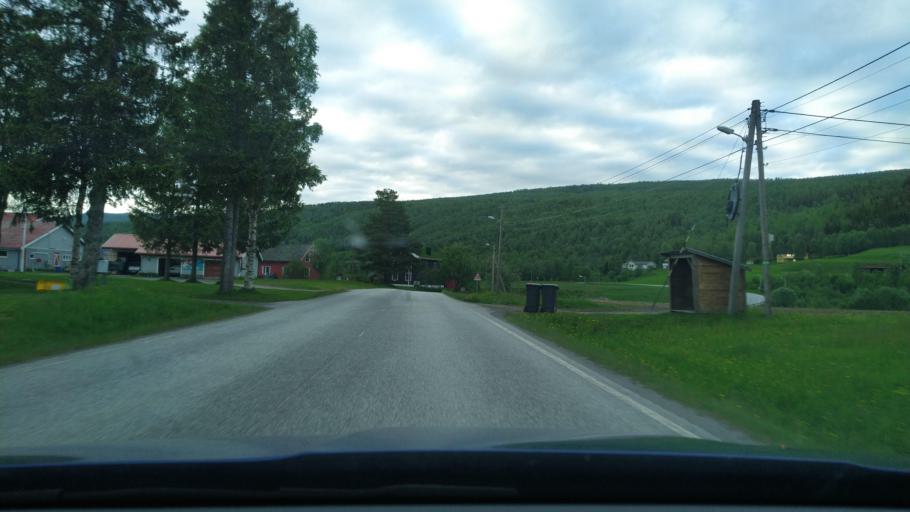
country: NO
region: Troms
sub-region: Sorreisa
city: Sorreisa
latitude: 69.1189
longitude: 18.2176
